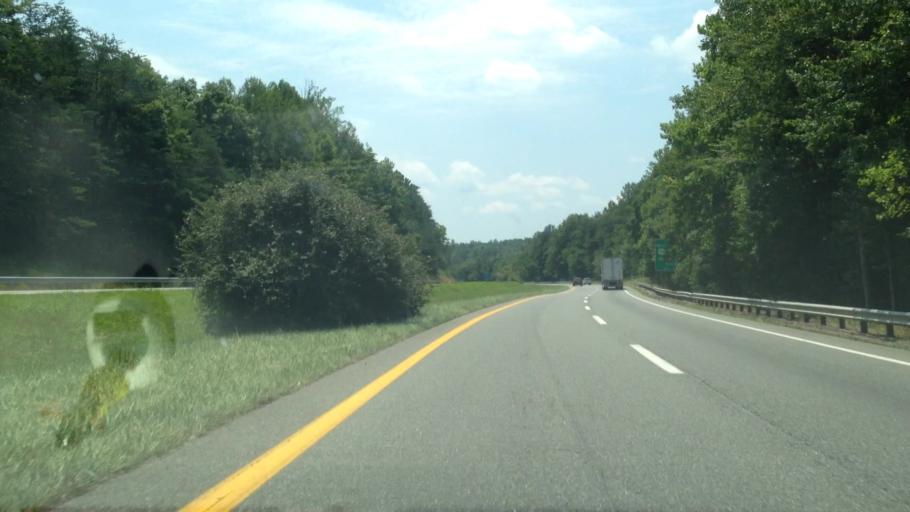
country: US
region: Virginia
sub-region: Henry County
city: Horse Pasture
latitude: 36.6641
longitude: -79.9271
